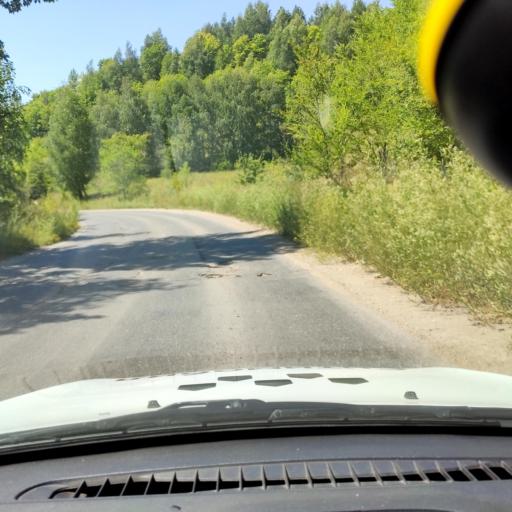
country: RU
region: Samara
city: Zhigulevsk
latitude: 53.4155
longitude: 49.5191
